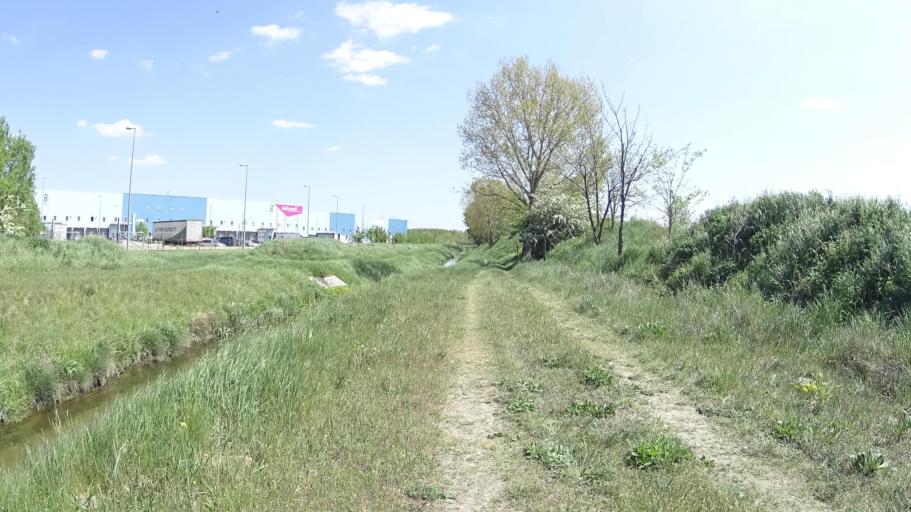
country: HU
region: Pest
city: Gyal
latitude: 47.3667
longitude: 19.2135
